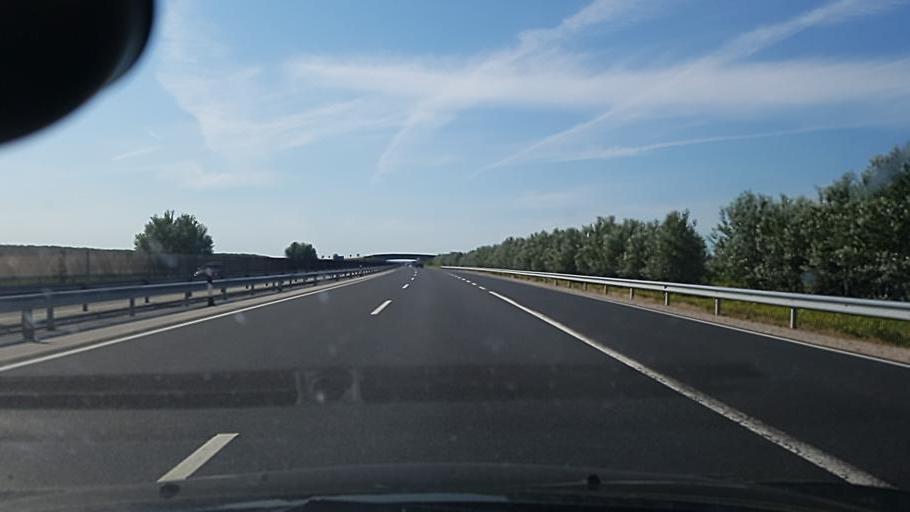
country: HU
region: Tolna
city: Szedres
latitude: 46.4373
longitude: 18.7112
